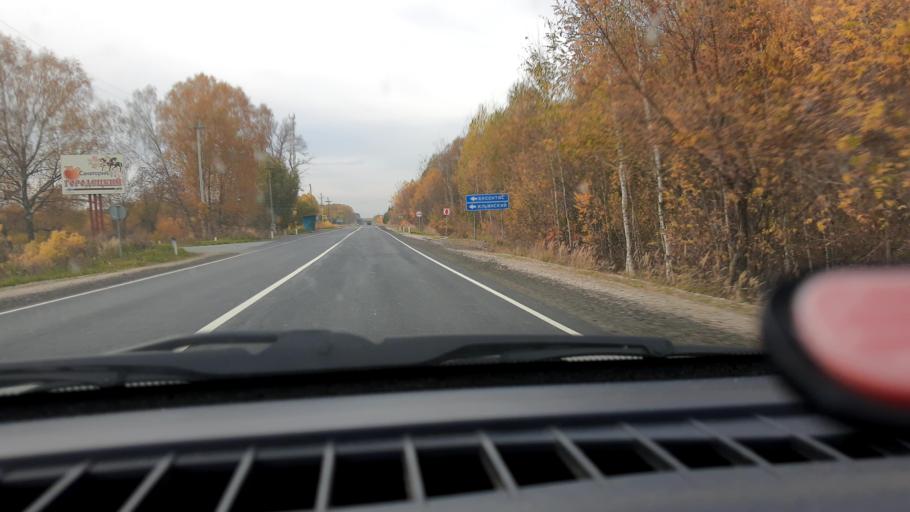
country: RU
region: Nizjnij Novgorod
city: Novaya Balakhna
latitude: 56.5975
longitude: 43.6420
